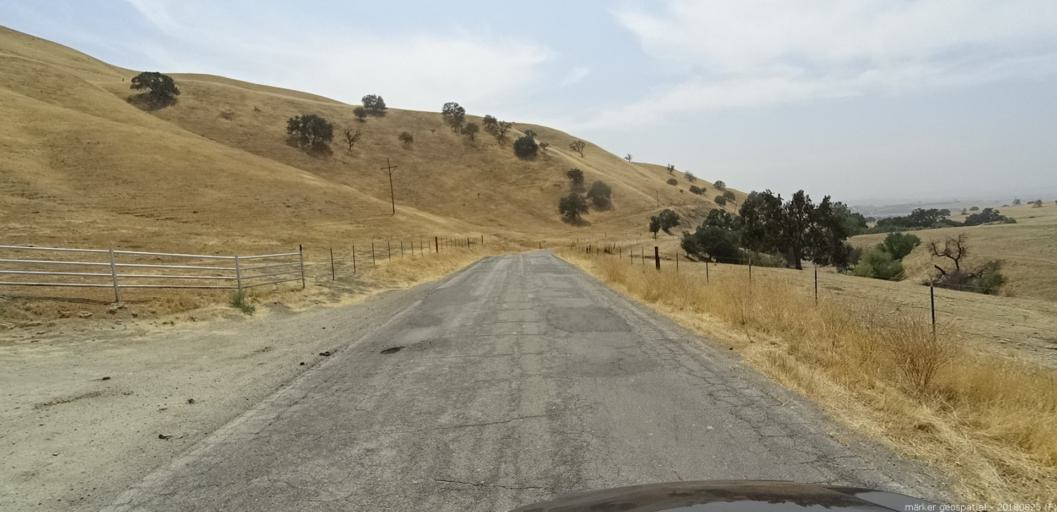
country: US
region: California
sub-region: San Luis Obispo County
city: San Miguel
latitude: 35.7870
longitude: -120.6835
